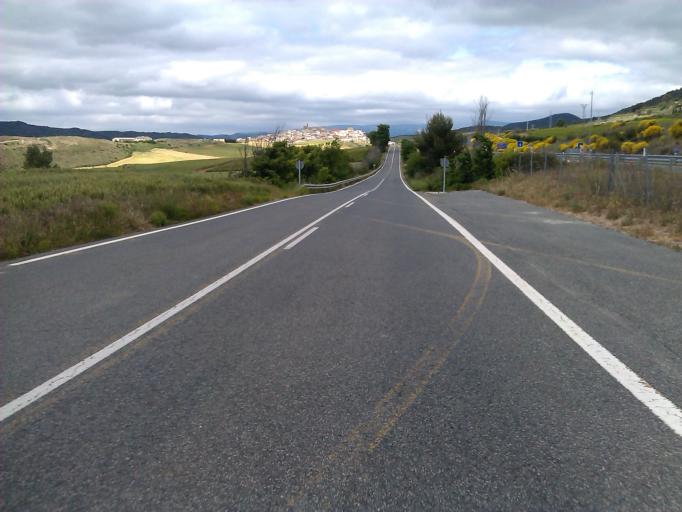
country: ES
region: Navarre
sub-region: Provincia de Navarra
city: Maneru
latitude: 42.6730
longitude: -1.8724
